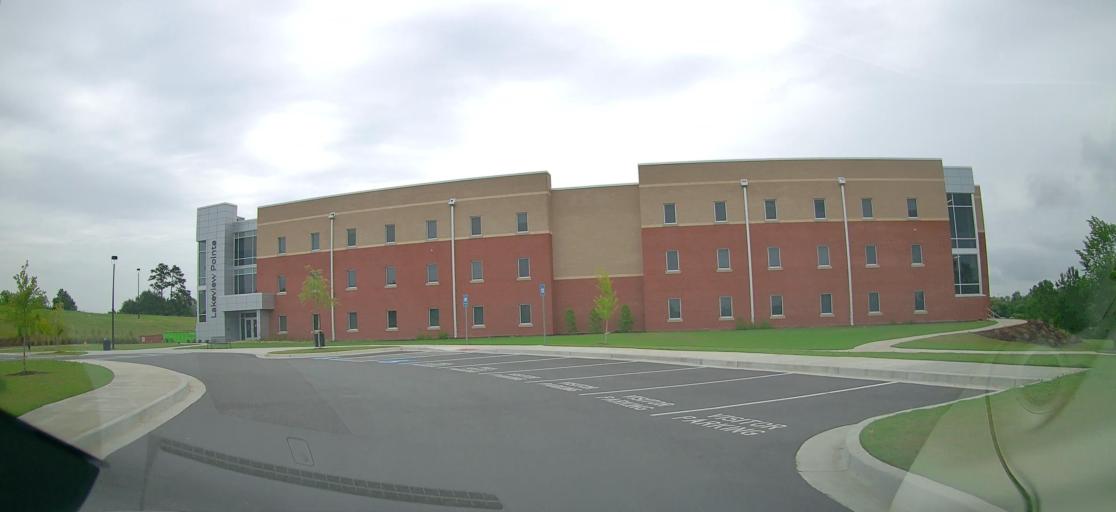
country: US
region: Georgia
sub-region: Bibb County
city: West Point
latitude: 32.8124
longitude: -83.7342
